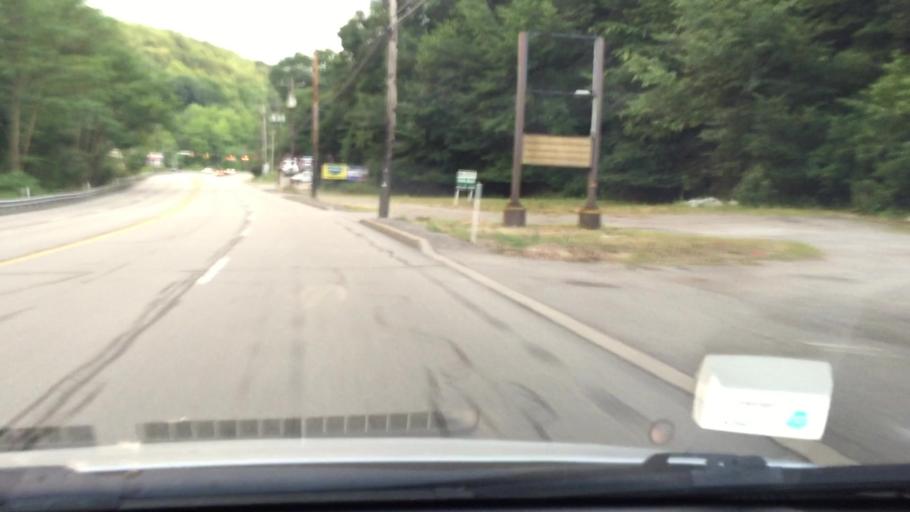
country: US
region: Pennsylvania
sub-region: Allegheny County
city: Allison Park
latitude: 40.5720
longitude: -79.9548
